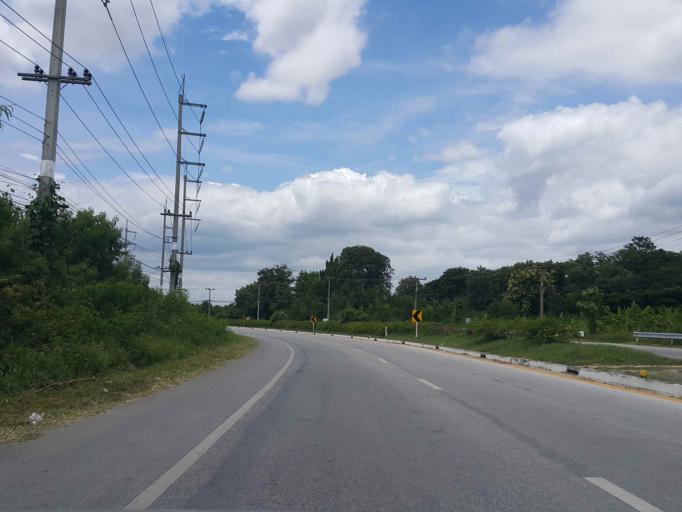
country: TH
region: Lamphun
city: Ban Hong
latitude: 18.3138
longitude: 98.8240
